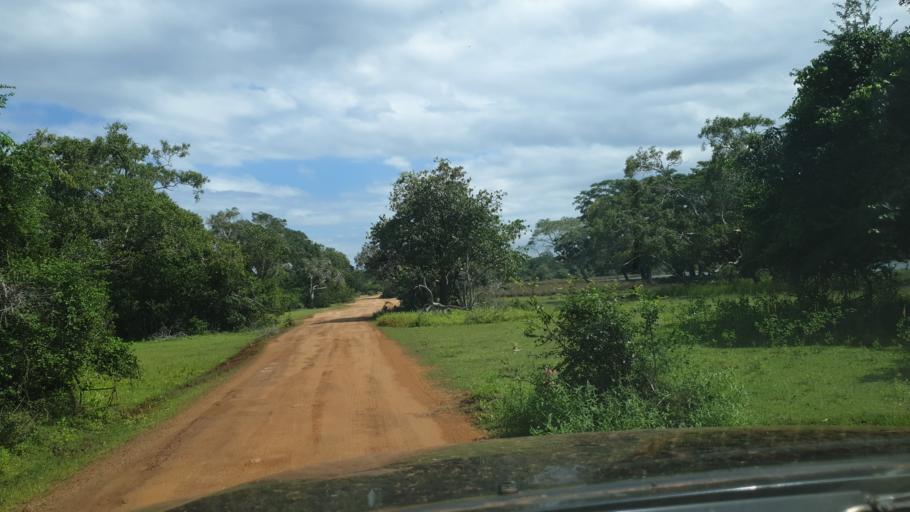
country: LK
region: North Central
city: Anuradhapura
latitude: 8.4220
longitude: 80.0071
